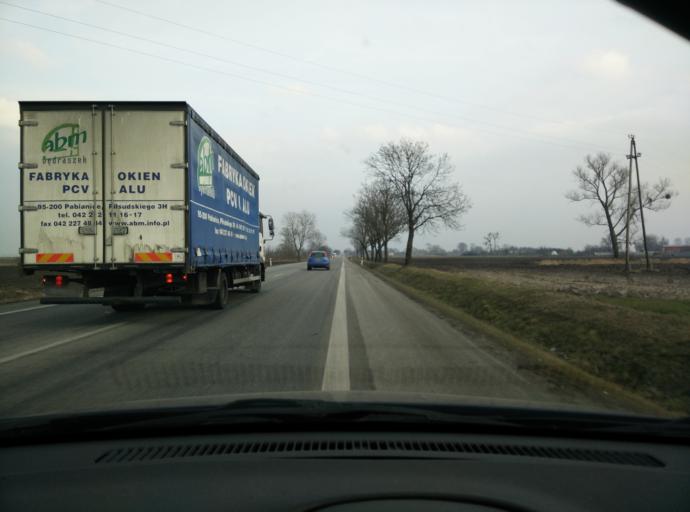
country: PL
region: Greater Poland Voivodeship
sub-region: Powiat poznanski
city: Kornik
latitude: 52.2399
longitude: 17.1500
